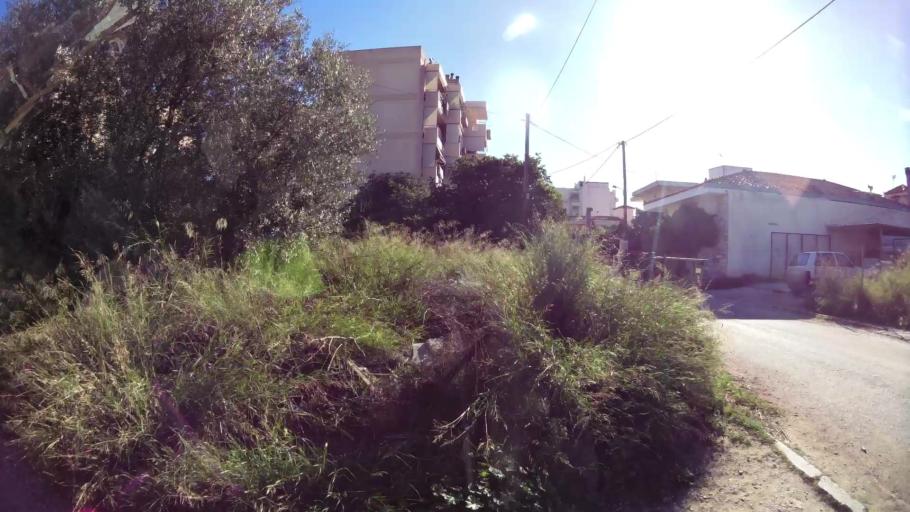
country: GR
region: Attica
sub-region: Nomarchia Anatolikis Attikis
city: Koropi
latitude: 37.9008
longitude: 23.8628
